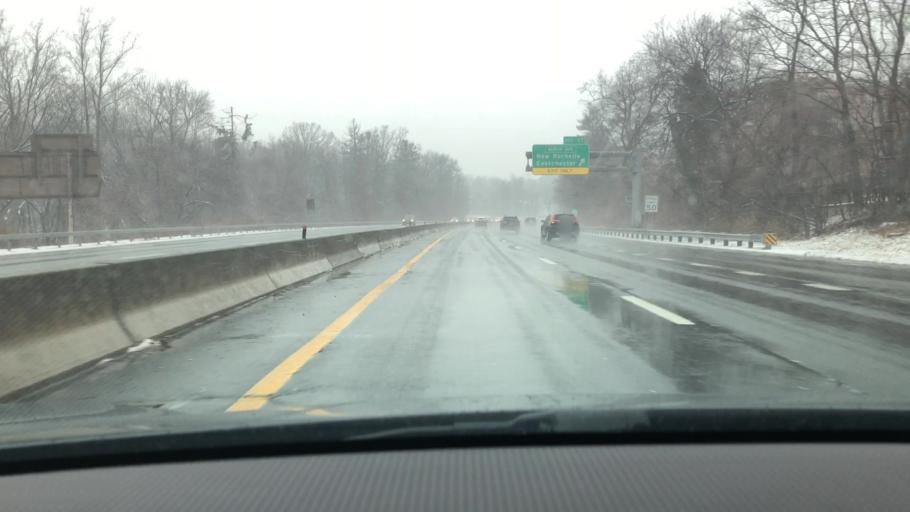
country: US
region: New York
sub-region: Westchester County
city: Tuckahoe
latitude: 40.9473
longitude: -73.7988
